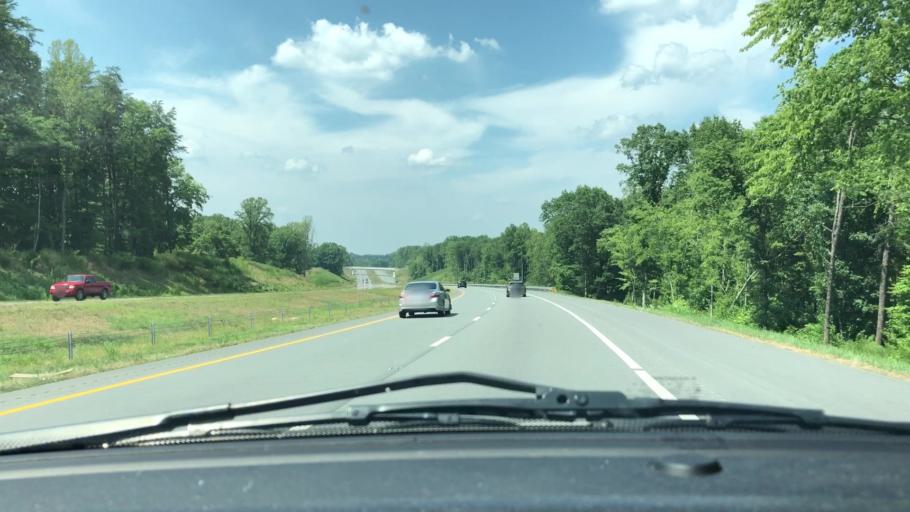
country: US
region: North Carolina
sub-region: Guilford County
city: Oak Ridge
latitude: 36.1438
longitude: -79.9587
